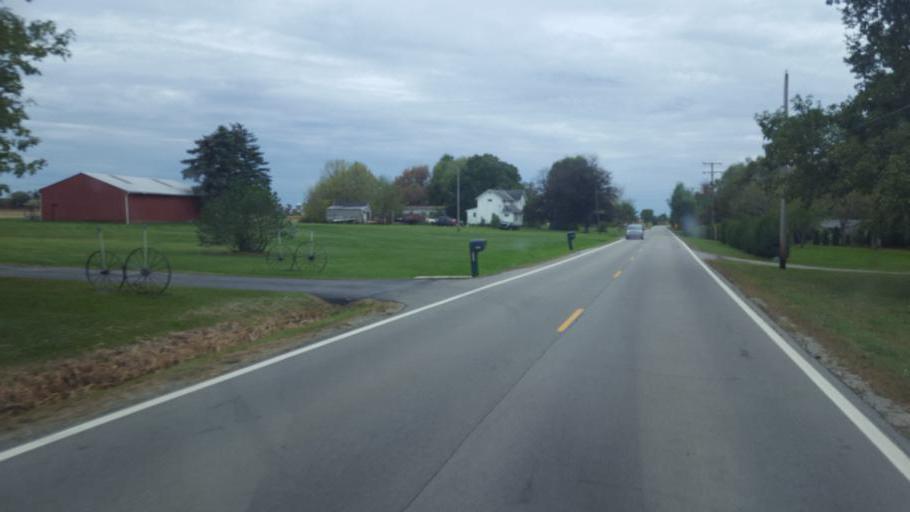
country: US
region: Ohio
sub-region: Huron County
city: Wakeman
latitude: 41.2840
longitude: -82.3807
